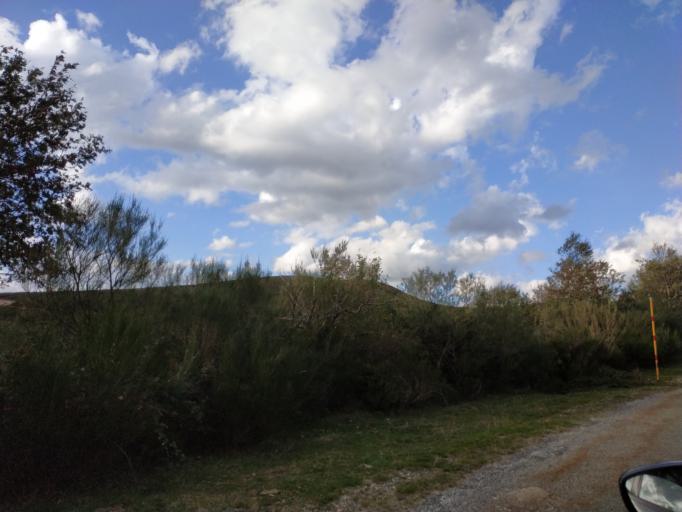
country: ES
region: Castille and Leon
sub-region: Provincia de Leon
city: Candin
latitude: 42.8788
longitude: -6.8302
